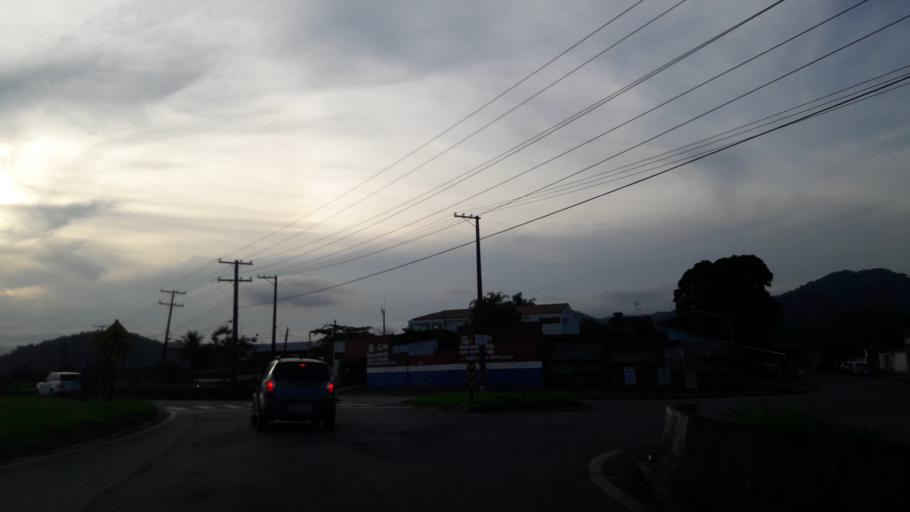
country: BR
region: Sao Paulo
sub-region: Peruibe
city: Peruibe
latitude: -24.2922
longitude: -47.0277
